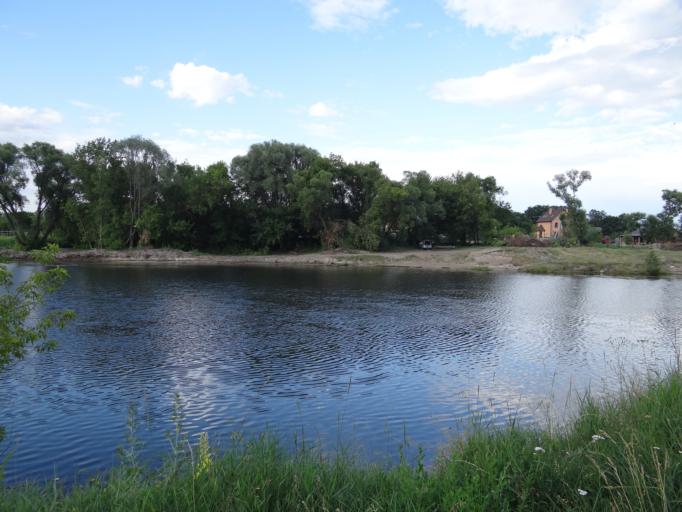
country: RU
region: Kursk
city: Voroshnevo
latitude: 51.6864
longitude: 36.0858
